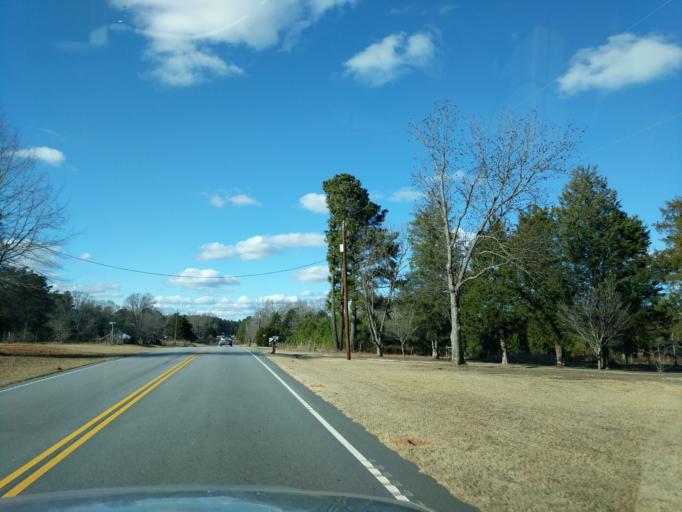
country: US
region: South Carolina
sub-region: Greenwood County
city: Ninety Six
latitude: 34.0916
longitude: -82.0951
